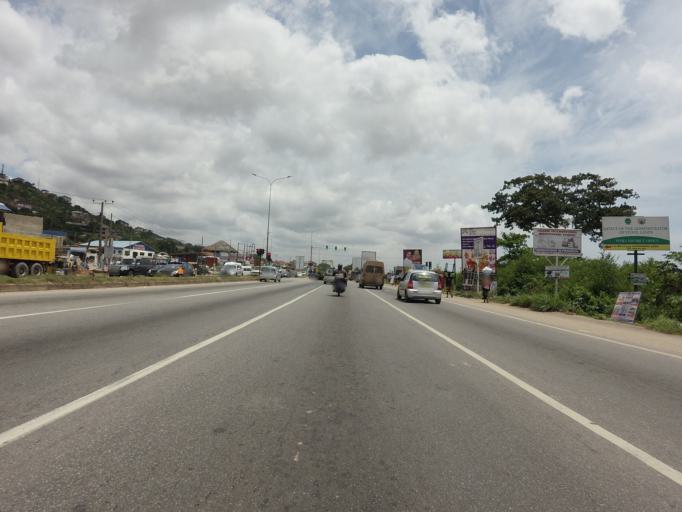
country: GH
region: Greater Accra
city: Gbawe
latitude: 5.5558
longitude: -0.3036
